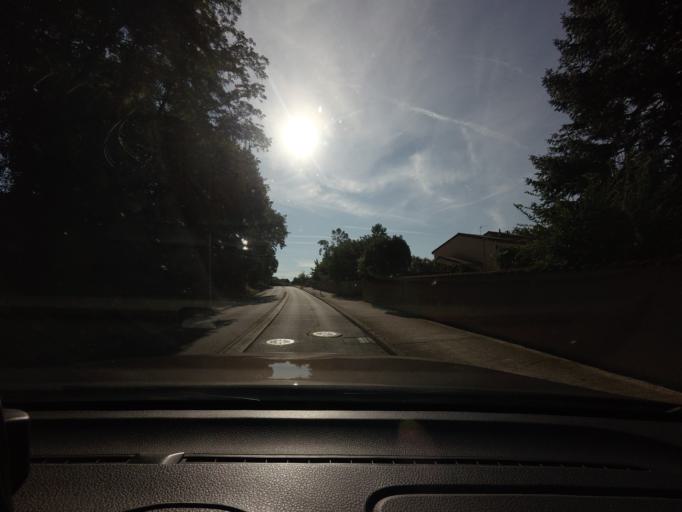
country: FR
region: Midi-Pyrenees
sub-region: Departement de la Haute-Garonne
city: Colomiers
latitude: 43.6200
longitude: 1.3157
